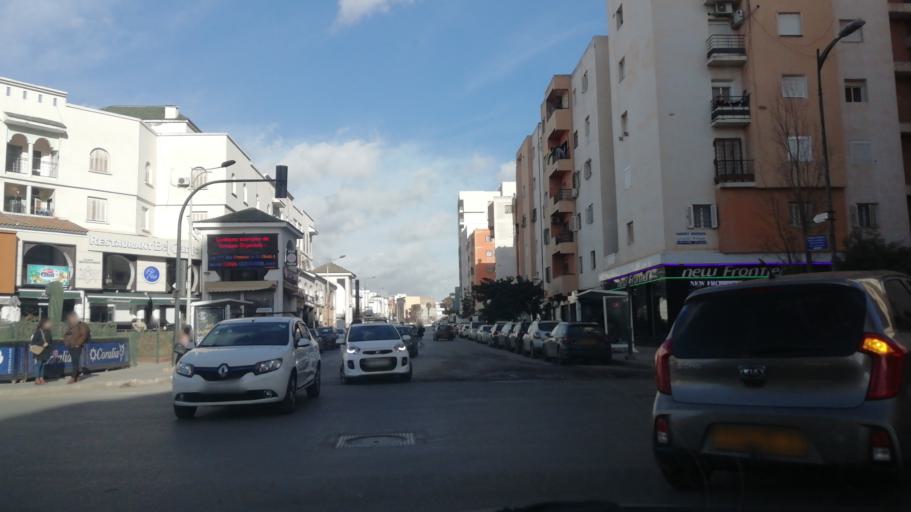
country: DZ
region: Oran
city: Bir el Djir
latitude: 35.7251
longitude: -0.5881
